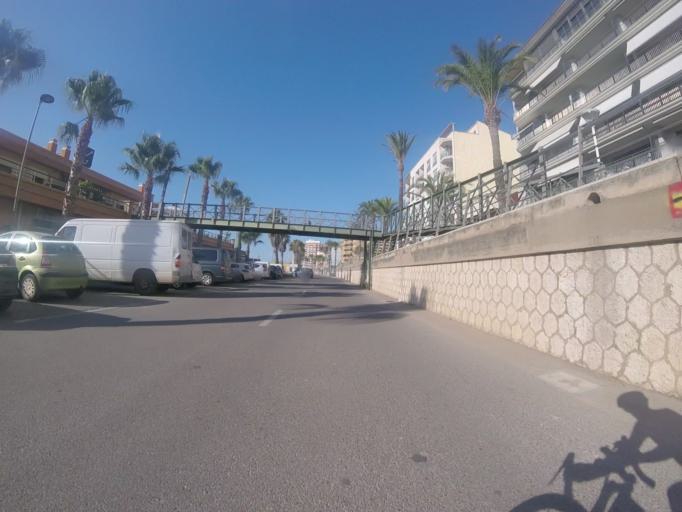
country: ES
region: Valencia
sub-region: Provincia de Castello
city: Benicarlo
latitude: 40.4155
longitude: 0.4326
